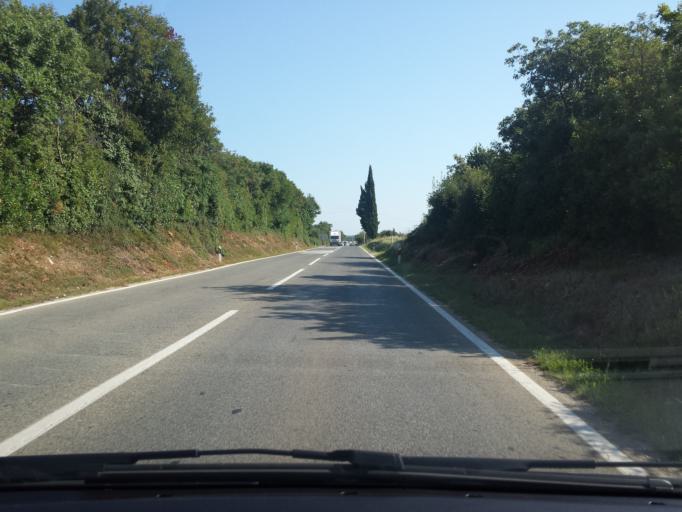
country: HR
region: Istarska
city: Galizana
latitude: 44.9100
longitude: 13.8481
